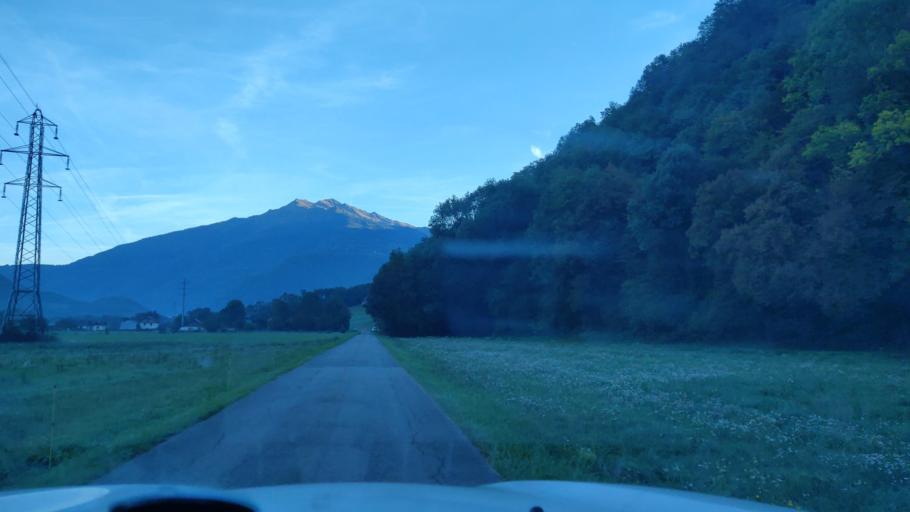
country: FR
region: Rhone-Alpes
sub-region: Departement de la Savoie
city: Saint-Remy-de-Maurienne
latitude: 45.4762
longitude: 6.2975
